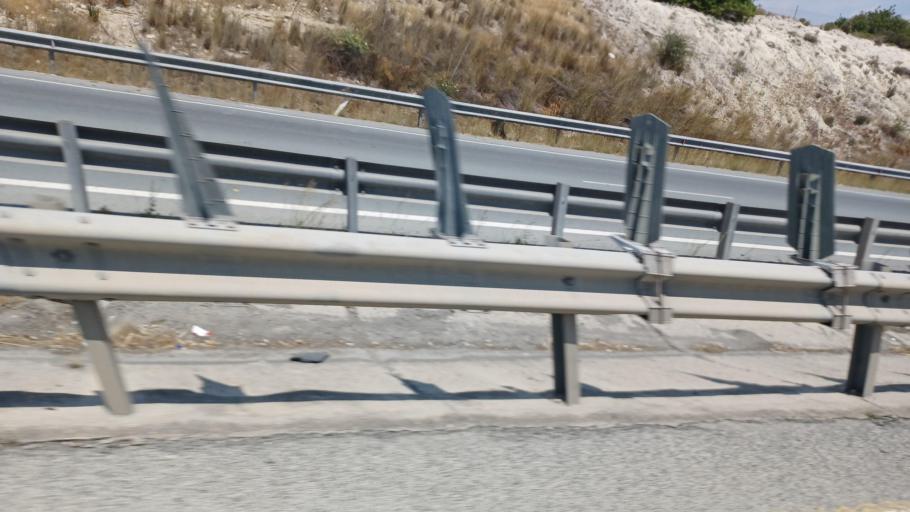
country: CY
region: Larnaka
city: Kofinou
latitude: 34.8114
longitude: 33.3537
